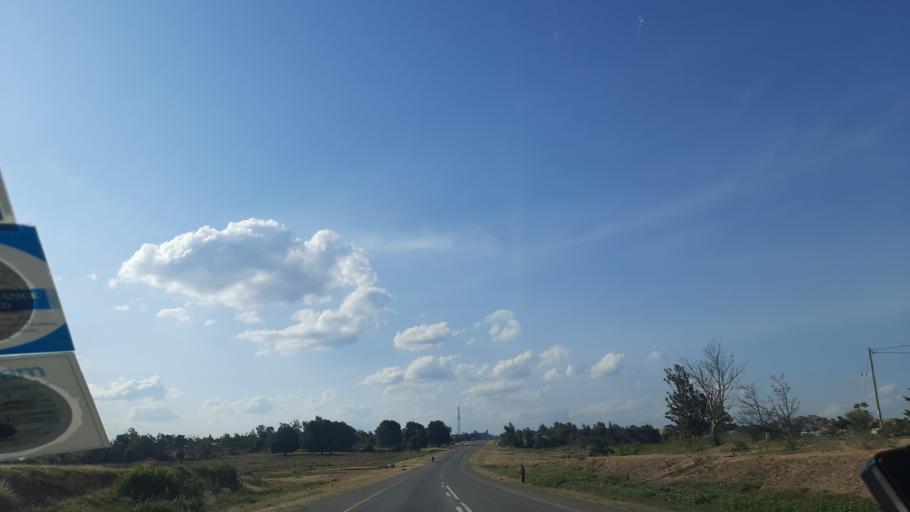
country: TZ
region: Singida
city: Puma
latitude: -5.0126
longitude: 34.7575
